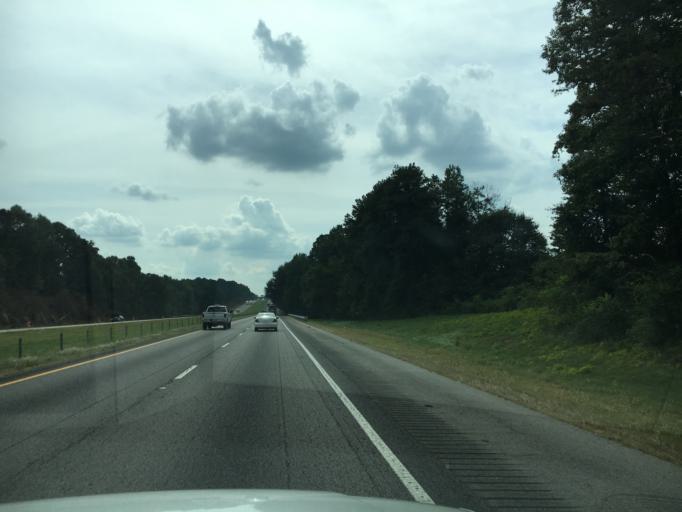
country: US
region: Georgia
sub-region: Banks County
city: Maysville
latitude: 34.2039
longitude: -83.5578
